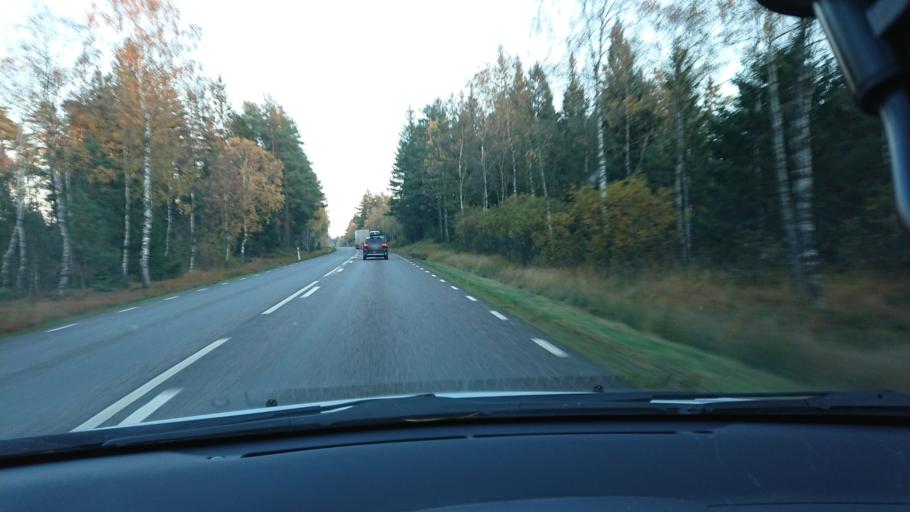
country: SE
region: Halland
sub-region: Laholms Kommun
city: Veinge
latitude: 56.7171
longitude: 13.1872
